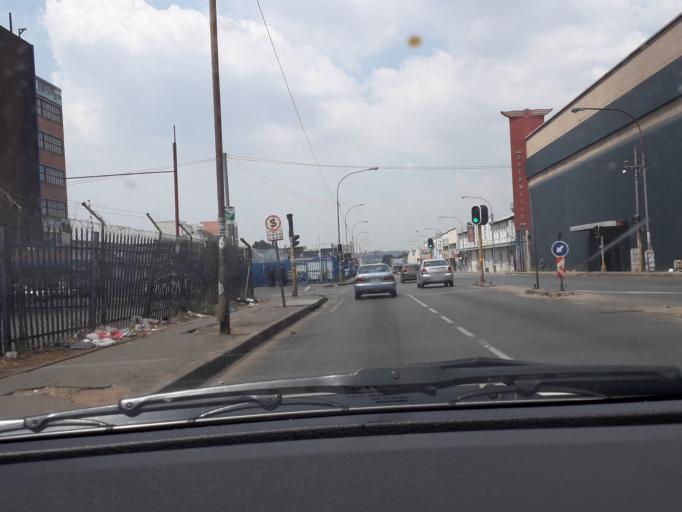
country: ZA
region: Gauteng
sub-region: City of Johannesburg Metropolitan Municipality
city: Johannesburg
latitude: -26.2153
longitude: 28.0437
